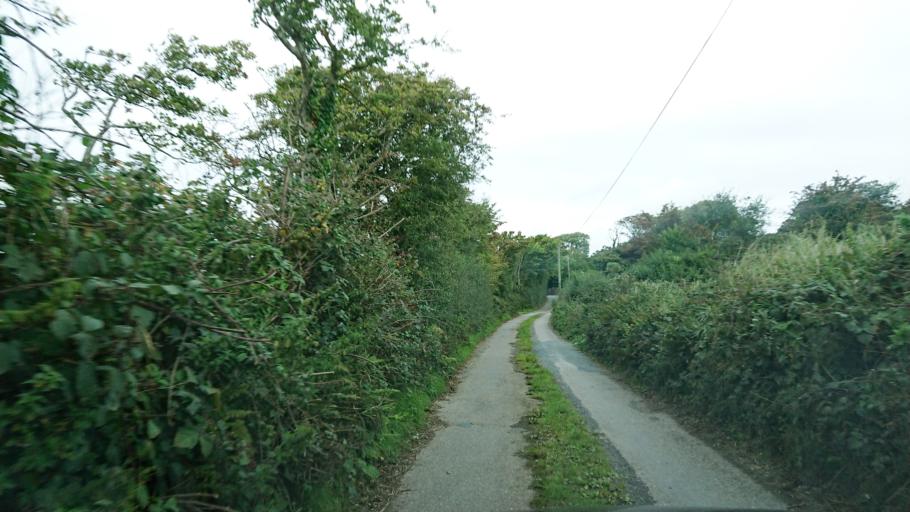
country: IE
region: Munster
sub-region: Waterford
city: Dunmore East
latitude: 52.2119
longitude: -7.0428
